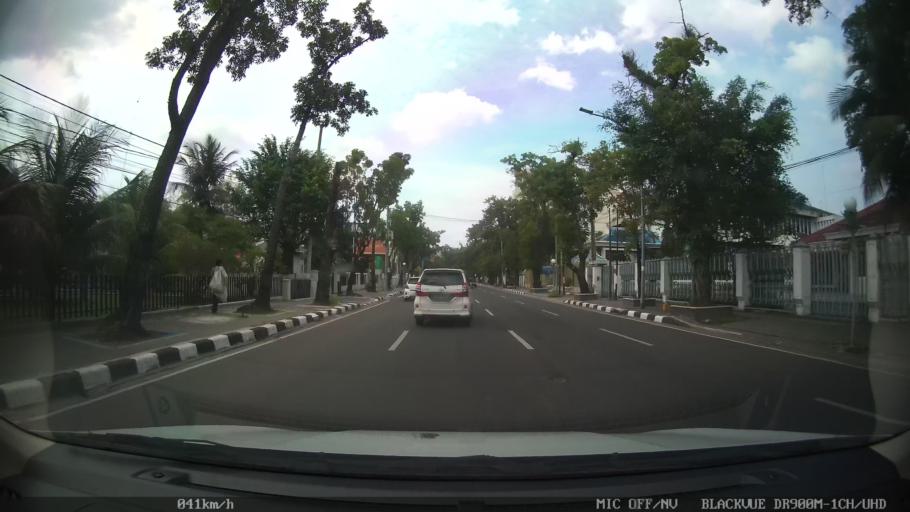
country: ID
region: North Sumatra
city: Medan
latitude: 3.5767
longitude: 98.6723
